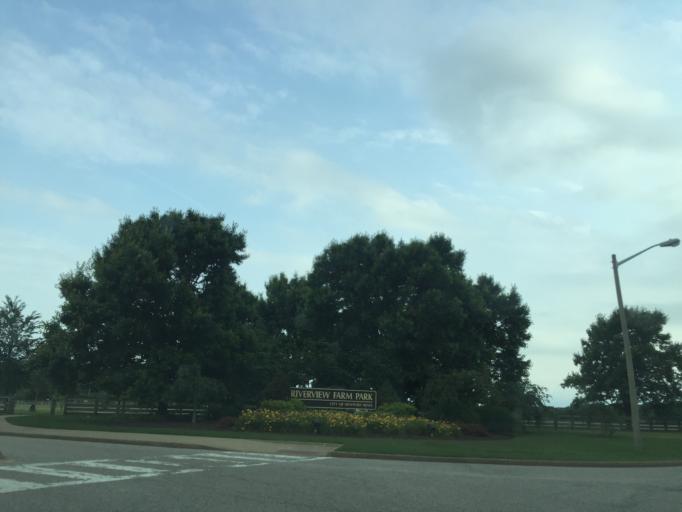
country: US
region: Virginia
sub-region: York County
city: Yorktown
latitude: 37.0948
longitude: -76.5283
